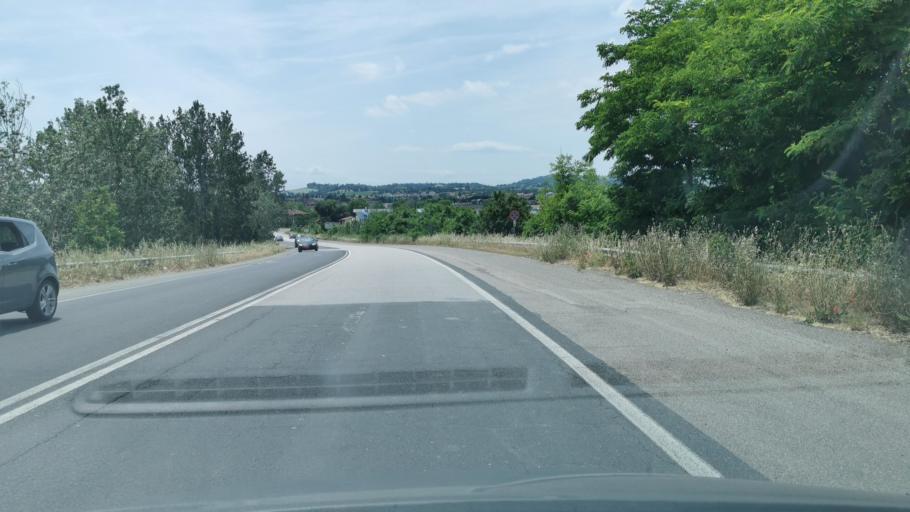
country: IT
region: Emilia-Romagna
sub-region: Provincia di Bologna
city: Castel San Pietro Terme
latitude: 44.4101
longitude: 11.5894
